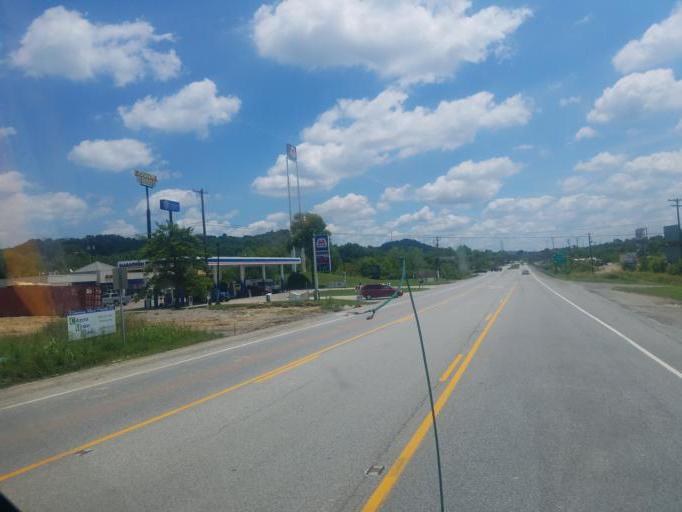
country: US
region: Kentucky
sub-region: Carroll County
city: Carrollton
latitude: 38.6500
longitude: -85.1250
